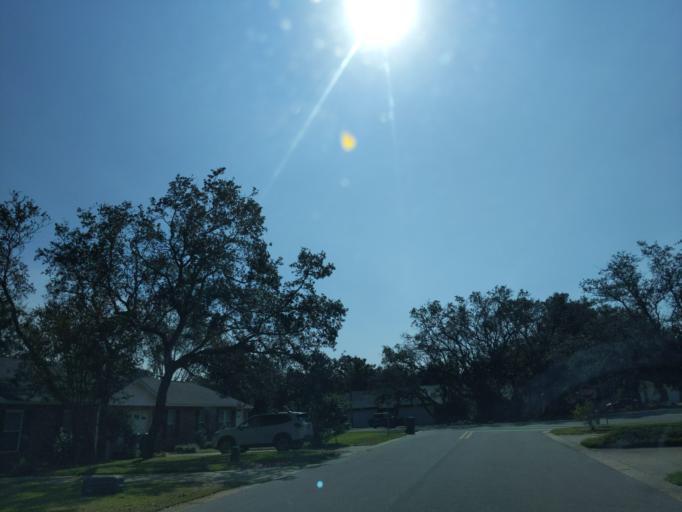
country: US
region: Florida
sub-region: Santa Rosa County
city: Gulf Breeze
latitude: 30.3621
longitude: -87.1721
